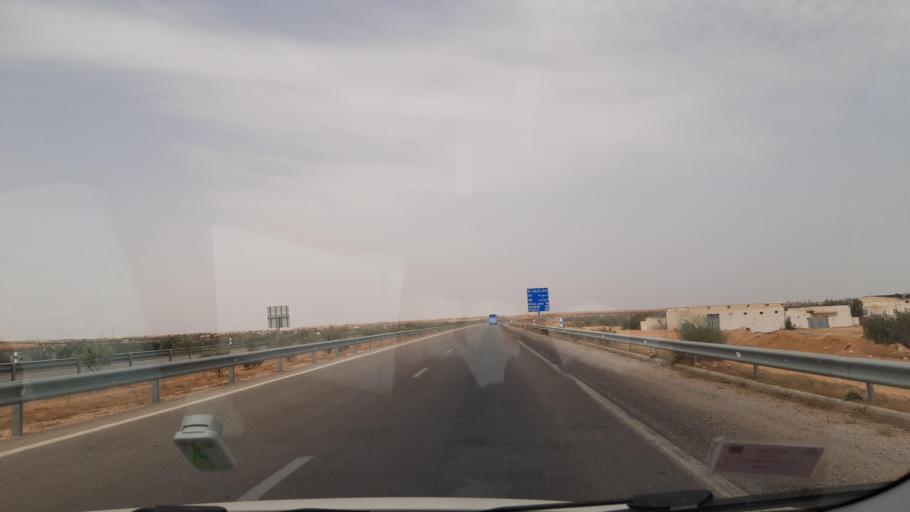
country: TN
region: Safaqis
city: Sfax
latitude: 34.7339
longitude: 10.5937
